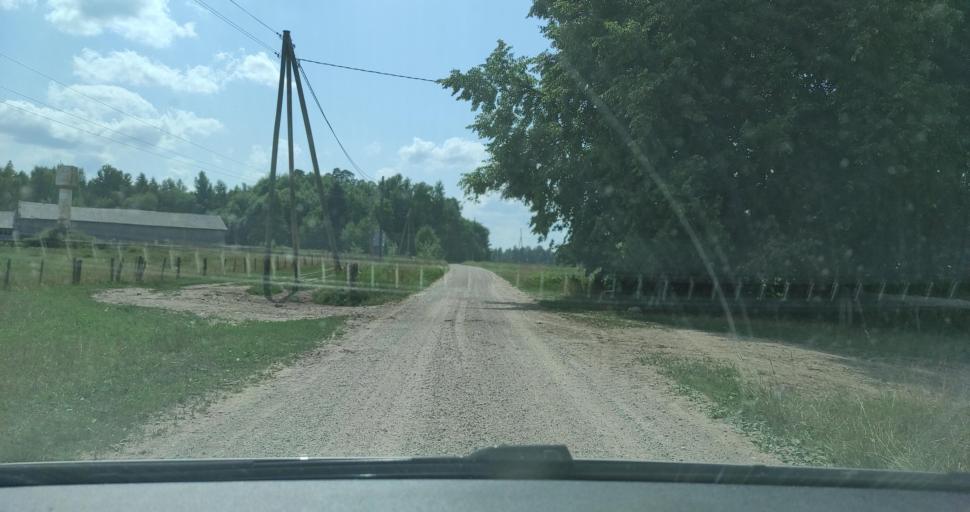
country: LV
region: Kuldigas Rajons
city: Kuldiga
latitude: 57.0599
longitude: 22.2435
